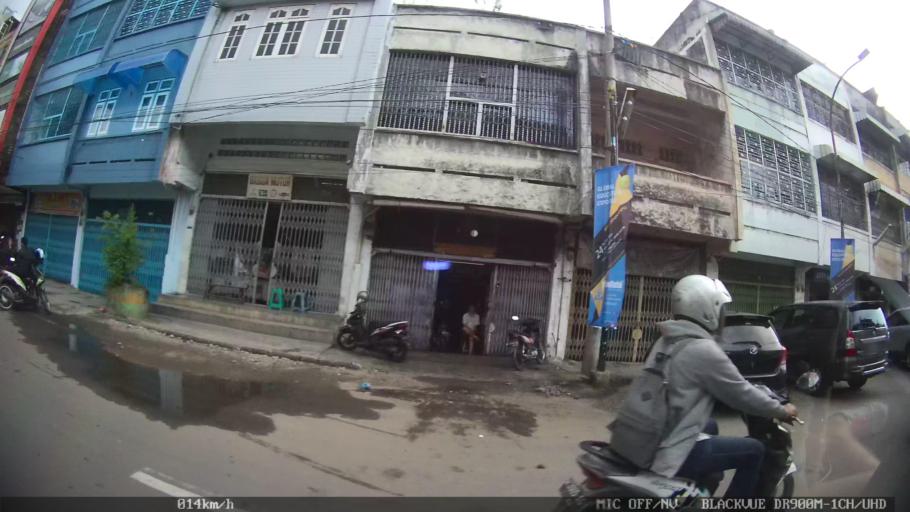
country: ID
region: North Sumatra
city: Medan
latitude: 3.5801
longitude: 98.6886
